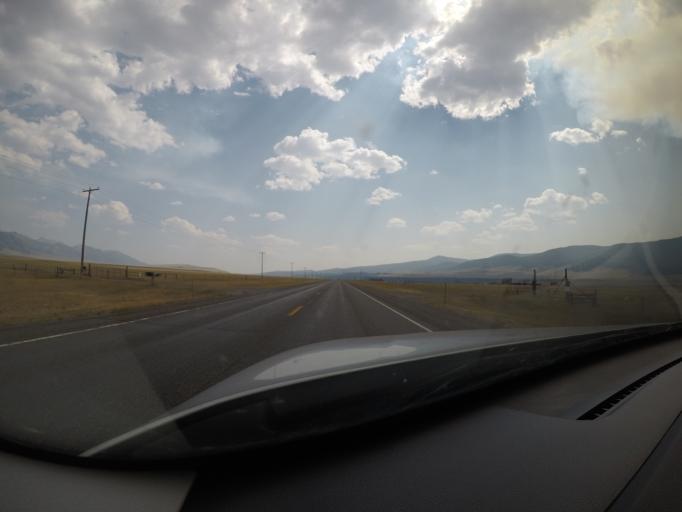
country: US
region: Montana
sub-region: Gallatin County
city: Big Sky
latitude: 45.0141
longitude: -111.6483
